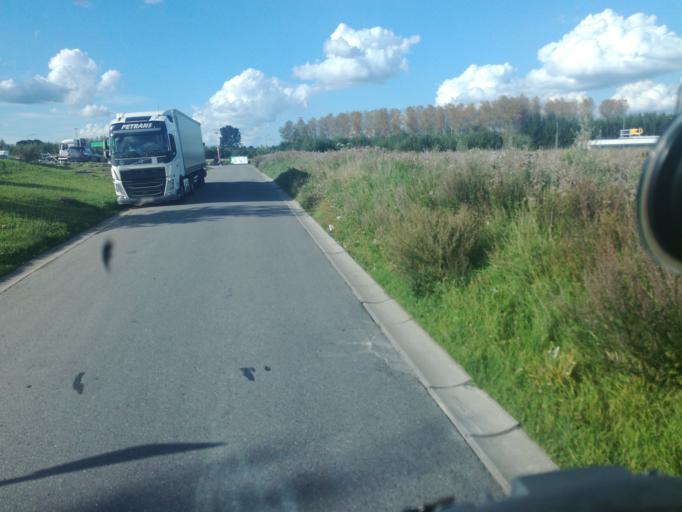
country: BE
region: Wallonia
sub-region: Province du Luxembourg
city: Habay-la-Vieille
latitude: 49.7024
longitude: 5.6273
